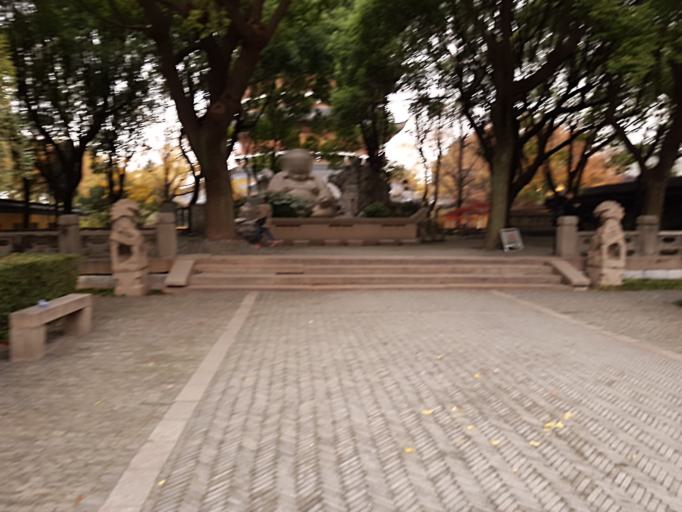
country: CN
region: Jiangsu Sheng
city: Pingjianglu
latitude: 31.3239
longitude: 120.6155
